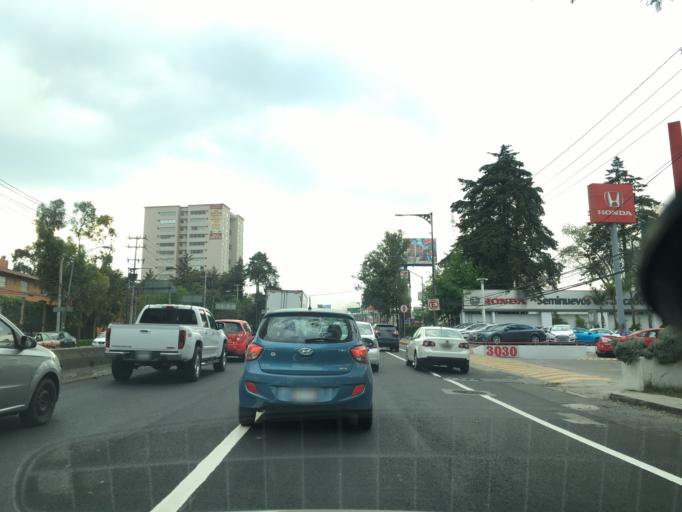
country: MX
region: Mexico City
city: Cuajimalpa
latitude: 19.3633
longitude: -99.2829
